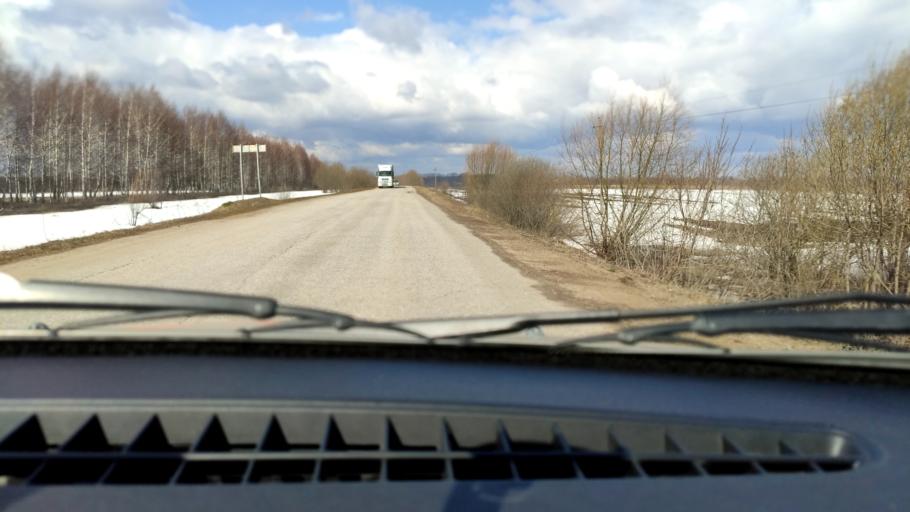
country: RU
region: Bashkortostan
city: Kudeyevskiy
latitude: 54.8548
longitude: 56.7878
